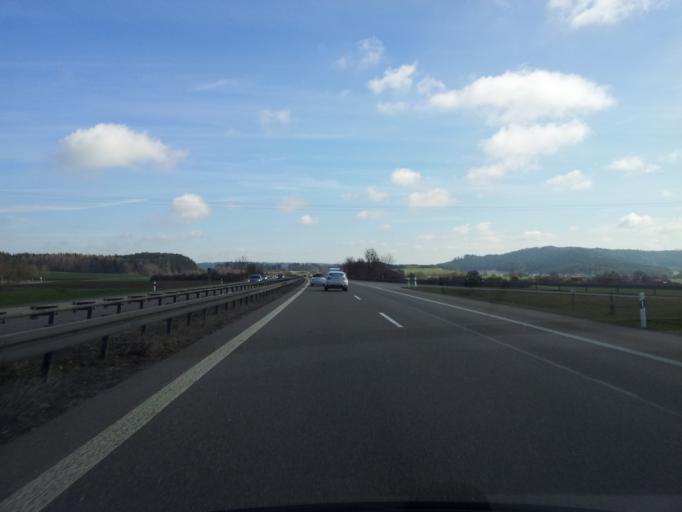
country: DE
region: Baden-Wuerttemberg
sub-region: Freiburg Region
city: Dietingen
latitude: 48.2076
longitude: 8.6275
